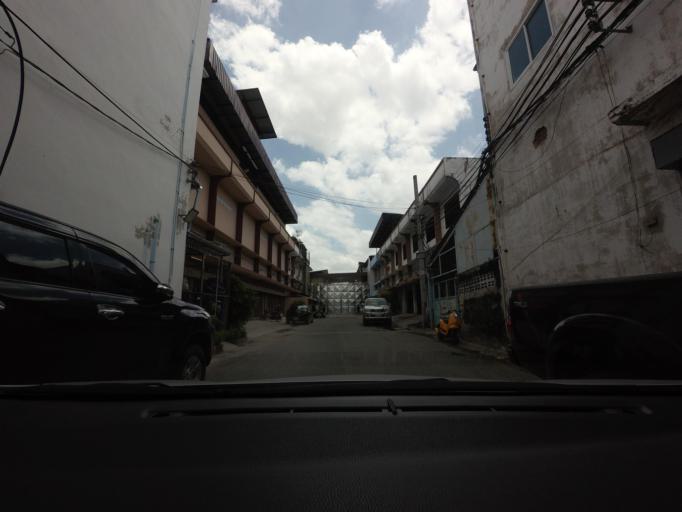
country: TH
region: Samut Prakan
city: Samut Prakan
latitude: 13.5682
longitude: 100.5908
